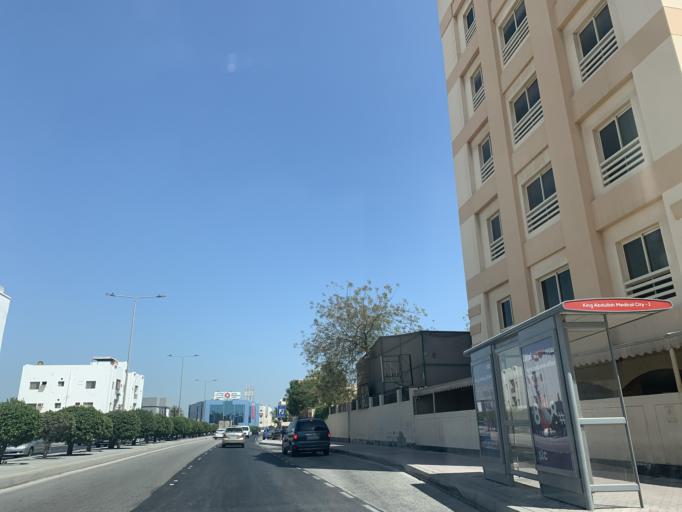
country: BH
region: Manama
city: Manama
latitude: 26.2126
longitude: 50.5672
